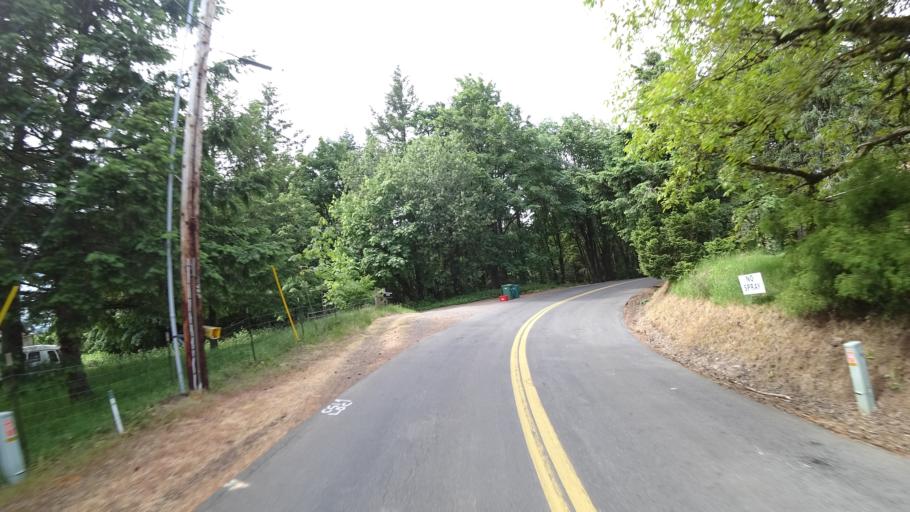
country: US
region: Oregon
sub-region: Washington County
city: Bethany
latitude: 45.6144
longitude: -122.8347
